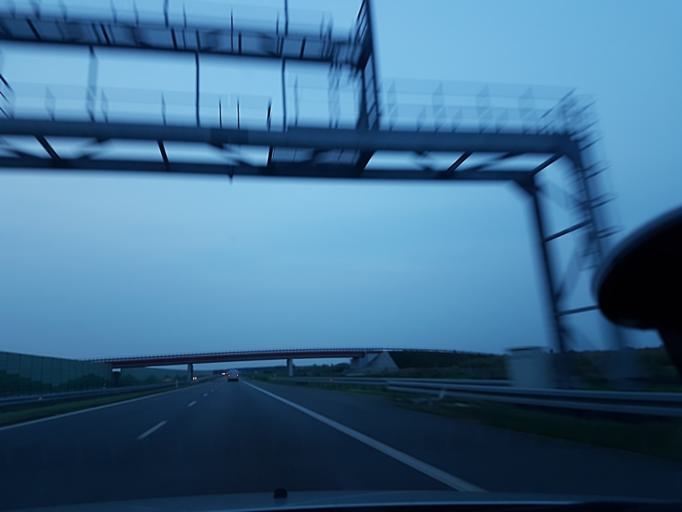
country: PL
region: Lodz Voivodeship
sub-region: Powiat leczycki
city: Piatek
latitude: 52.0850
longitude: 19.5254
